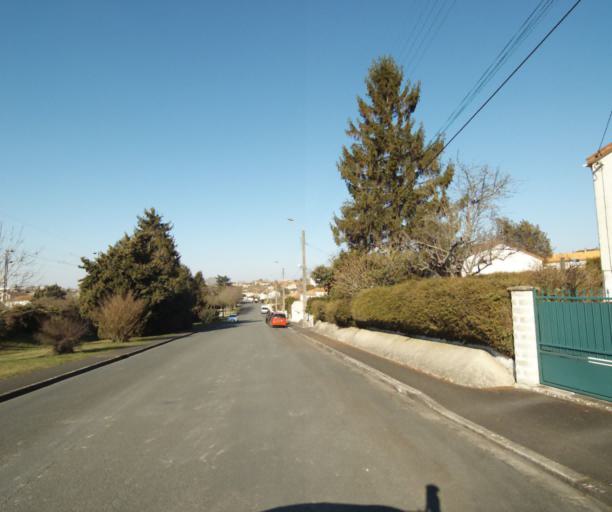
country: FR
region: Poitou-Charentes
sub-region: Departement des Deux-Sevres
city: Niort
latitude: 46.3212
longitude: -0.4338
